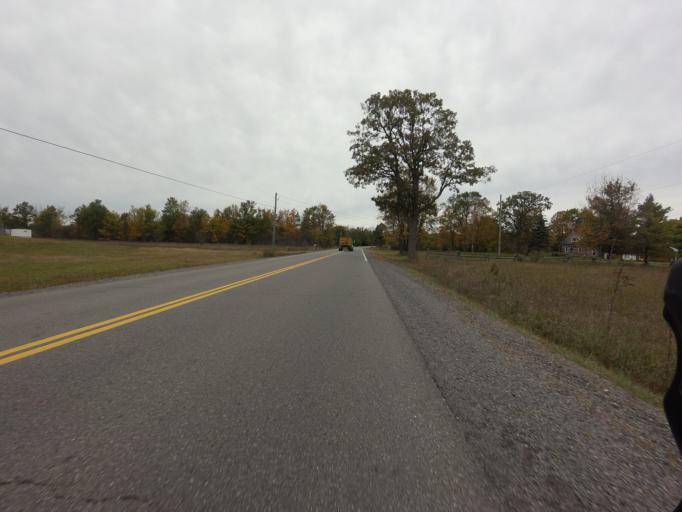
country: CA
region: Ontario
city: Brockville
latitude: 44.7955
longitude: -75.7872
